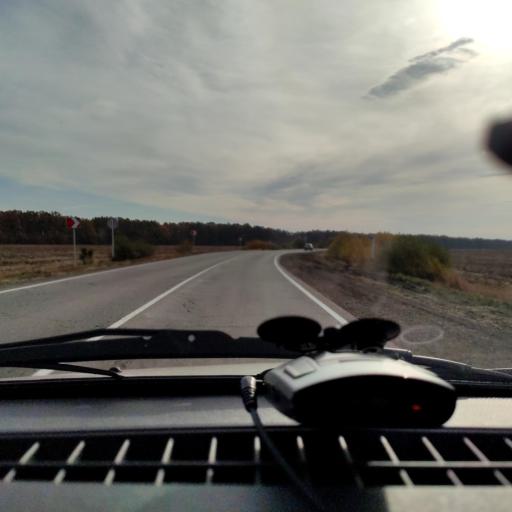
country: RU
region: Voronezj
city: Shilovo
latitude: 51.4513
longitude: 38.9881
